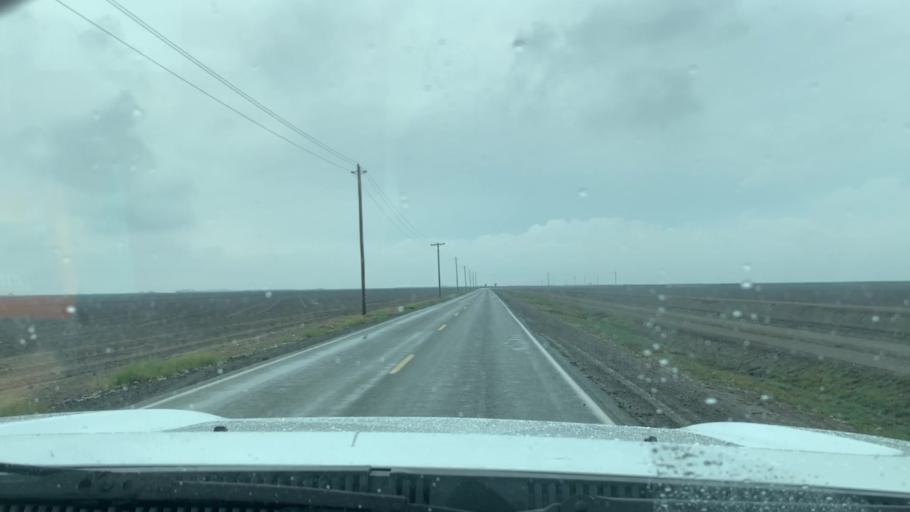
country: US
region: California
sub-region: Tulare County
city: Alpaugh
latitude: 35.9683
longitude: -119.5720
